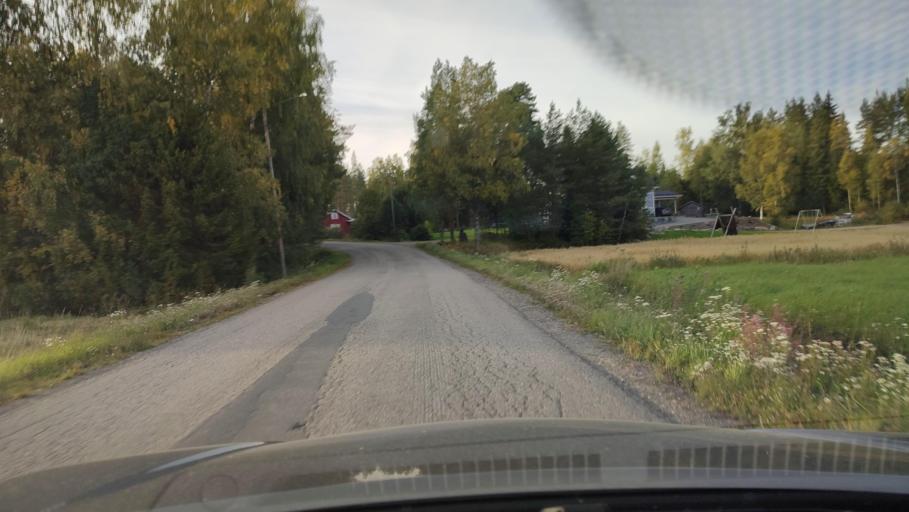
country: FI
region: Southern Ostrobothnia
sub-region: Suupohja
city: Karijoki
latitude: 62.1460
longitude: 21.5615
